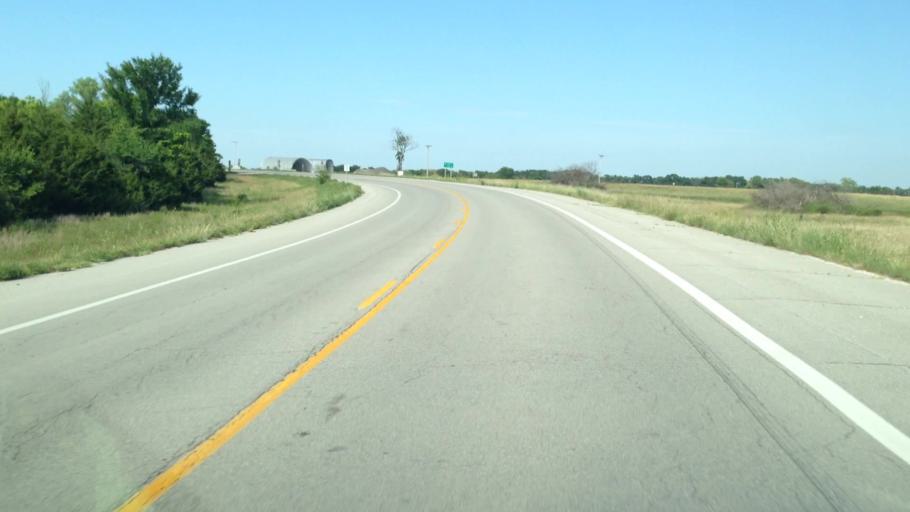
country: US
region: Kansas
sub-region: Neosho County
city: Erie
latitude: 37.6890
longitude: -95.1635
